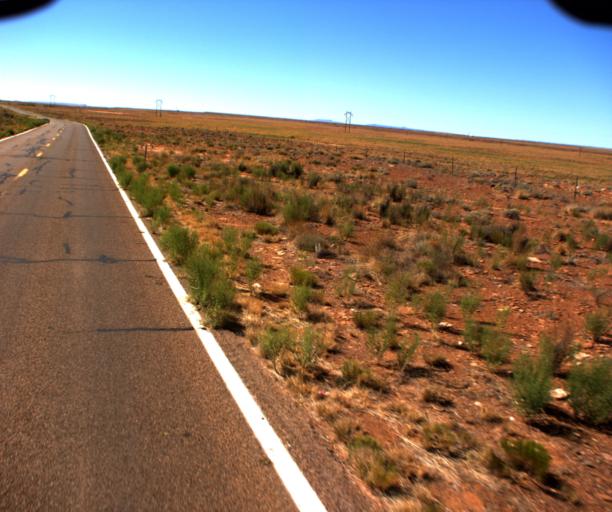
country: US
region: Arizona
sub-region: Coconino County
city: LeChee
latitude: 35.2634
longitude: -110.9700
